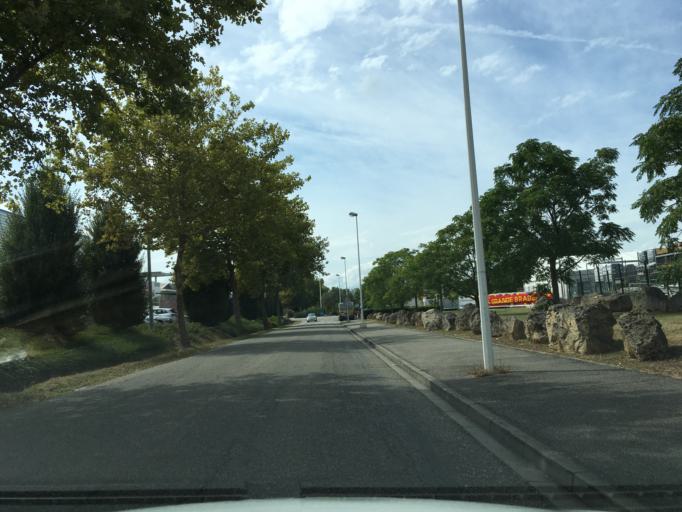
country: FR
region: Aquitaine
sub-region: Departement du Lot-et-Garonne
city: Agen
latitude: 44.1832
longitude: 0.6205
